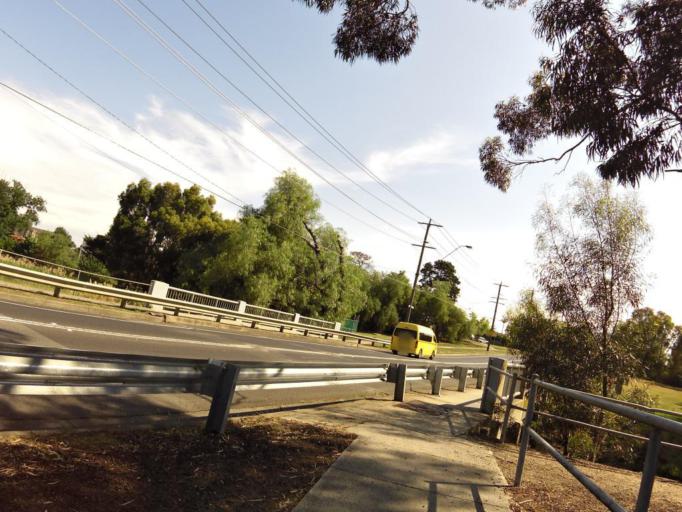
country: AU
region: Victoria
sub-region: Whittlesea
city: Epping
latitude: -37.6486
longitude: 145.0337
